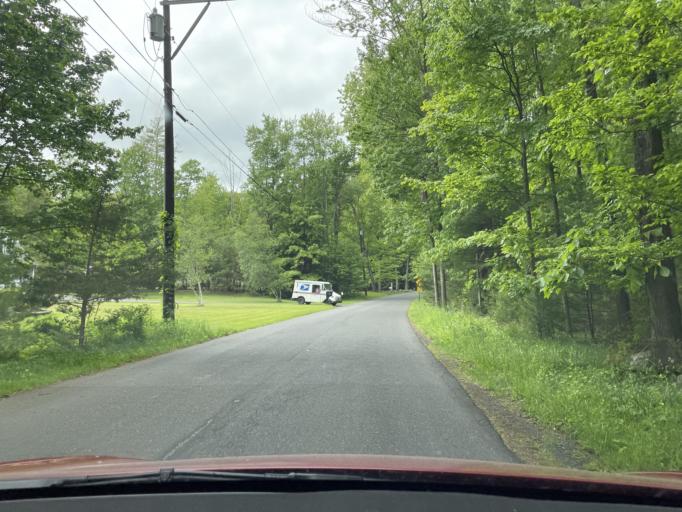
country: US
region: New York
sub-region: Ulster County
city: West Hurley
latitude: 42.0150
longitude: -74.0993
